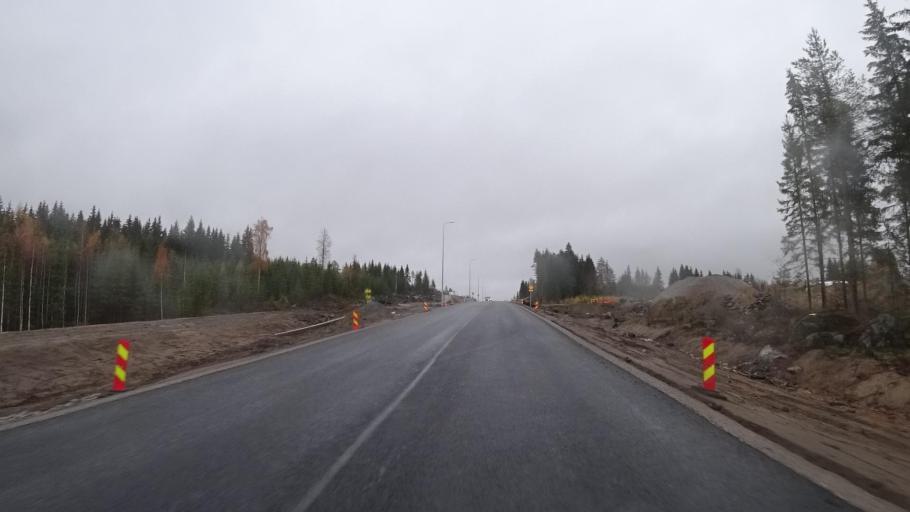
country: FI
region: Northern Savo
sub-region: Varkaus
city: Kangaslampi
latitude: 62.3898
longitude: 28.1416
